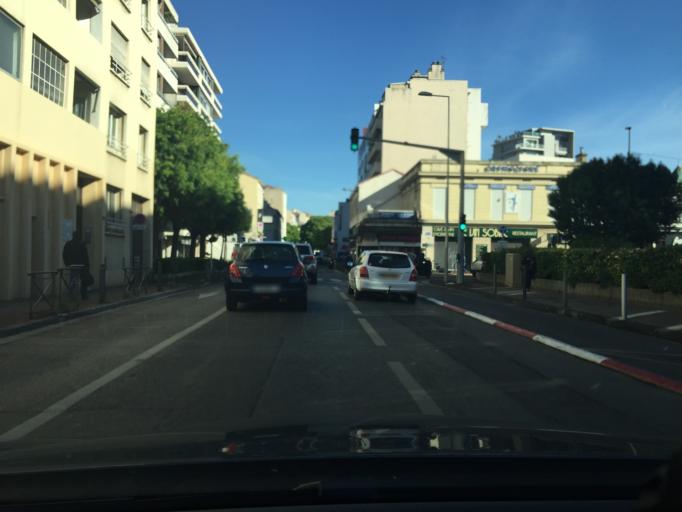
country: FR
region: Provence-Alpes-Cote d'Azur
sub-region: Departement des Bouches-du-Rhone
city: Marseille 08
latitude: 43.2686
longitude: 5.3887
